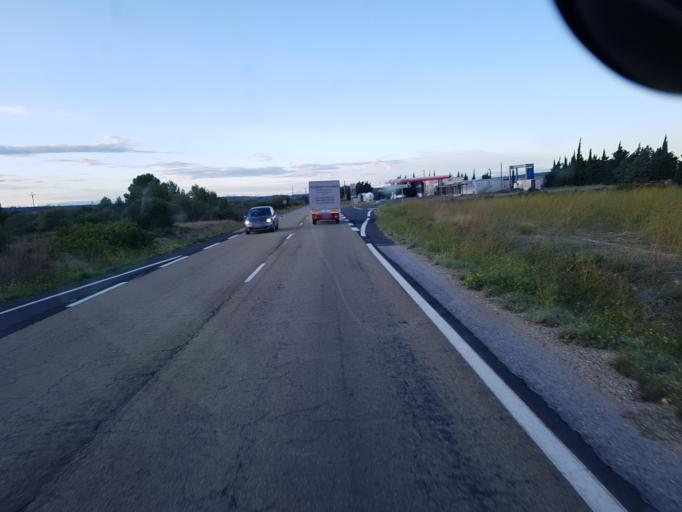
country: FR
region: Languedoc-Roussillon
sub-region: Departement de l'Aude
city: Leucate
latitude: 42.9440
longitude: 2.9890
